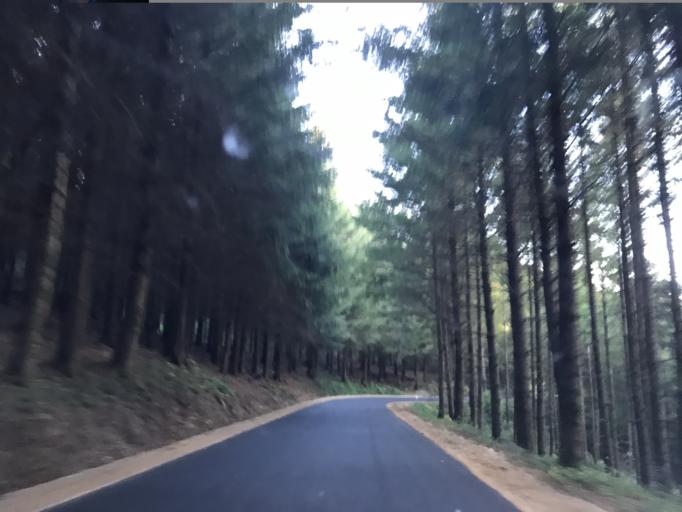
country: FR
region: Auvergne
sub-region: Departement du Puy-de-Dome
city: Celles-sur-Durolle
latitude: 45.8129
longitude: 3.6609
